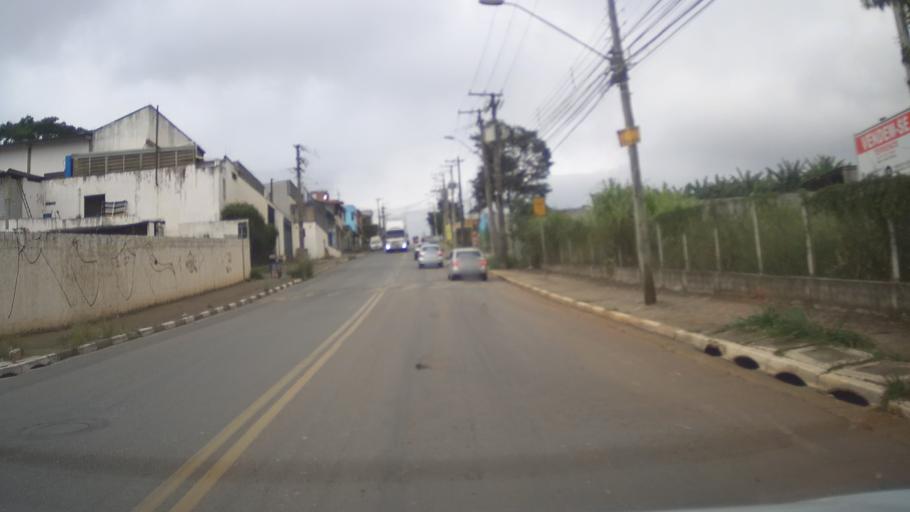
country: BR
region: Sao Paulo
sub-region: Aruja
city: Aruja
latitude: -23.4092
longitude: -46.3871
